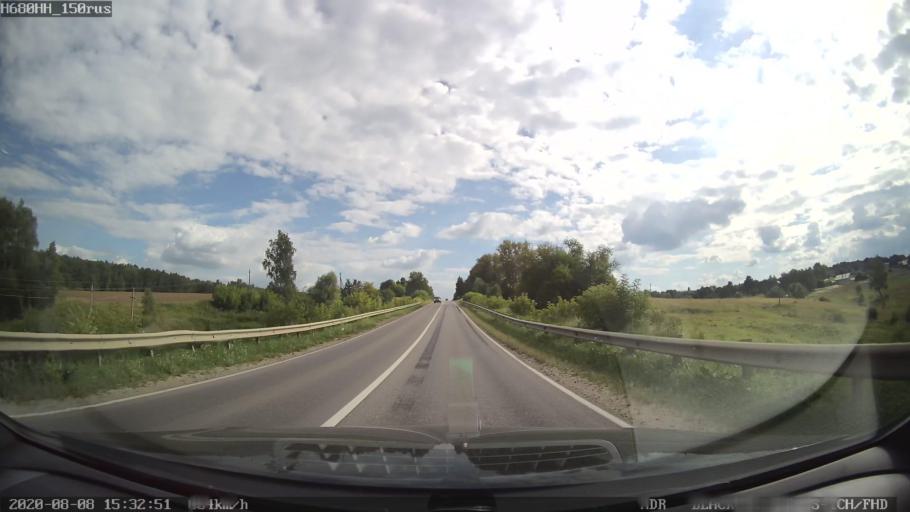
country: RU
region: Tula
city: Zaokskiy
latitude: 54.7792
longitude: 37.4347
